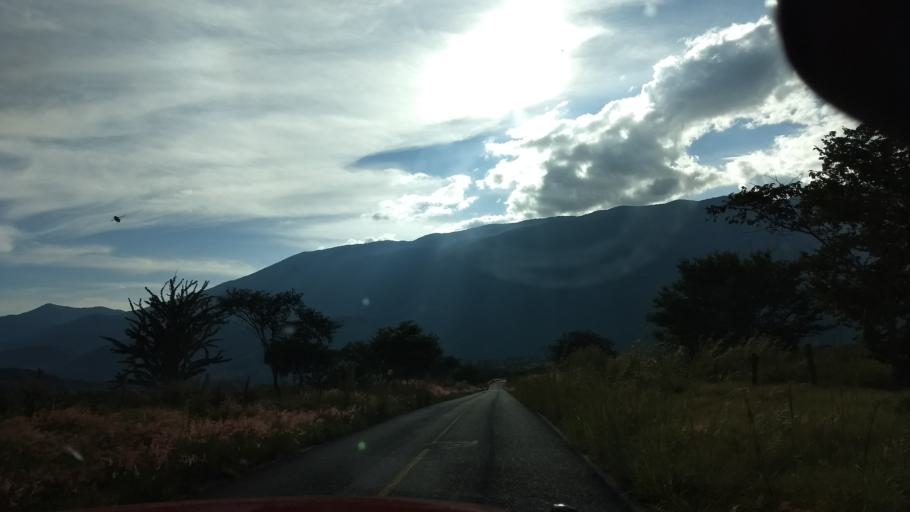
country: MX
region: Colima
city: Suchitlan
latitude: 19.4546
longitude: -103.8053
